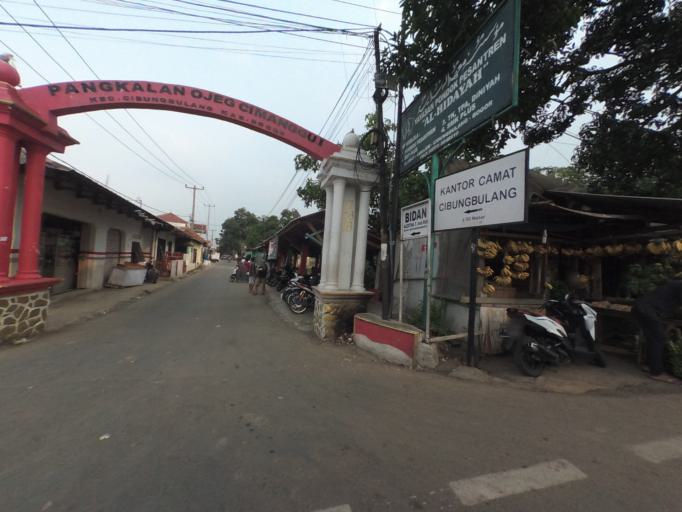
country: ID
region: West Java
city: Ciampea
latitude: -6.5739
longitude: 106.6661
